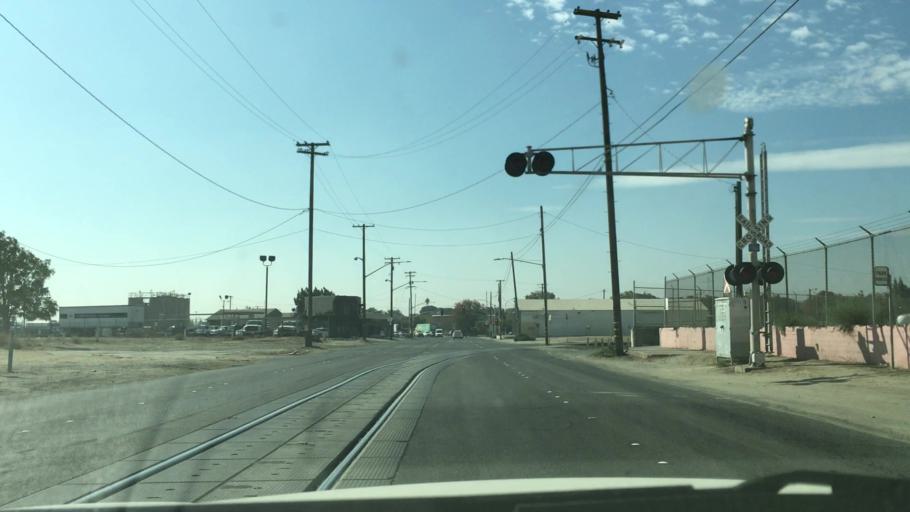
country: US
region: California
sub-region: Stanislaus County
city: Modesto
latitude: 37.6317
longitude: -120.9926
